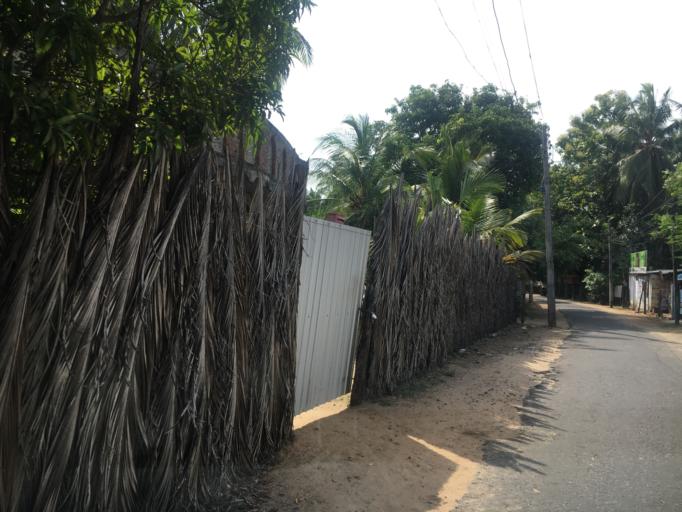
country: LK
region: Eastern Province
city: Batticaloa
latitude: 7.7433
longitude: 81.6921
